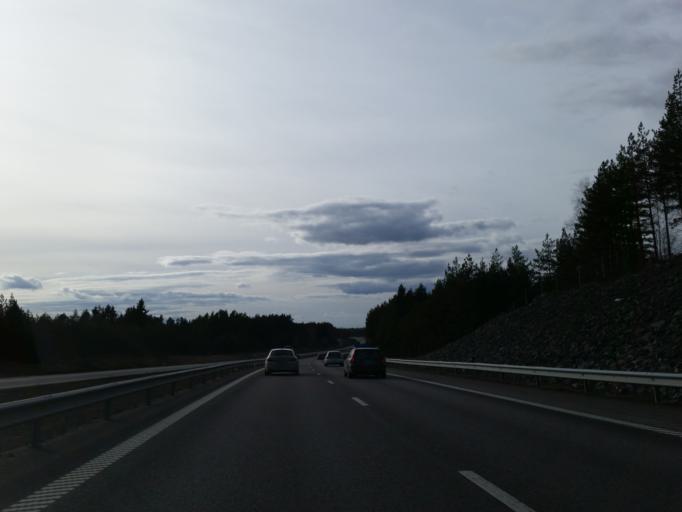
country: SE
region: Soedermanland
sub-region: Nykopings Kommun
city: Olstorp
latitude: 58.7548
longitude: 16.6442
